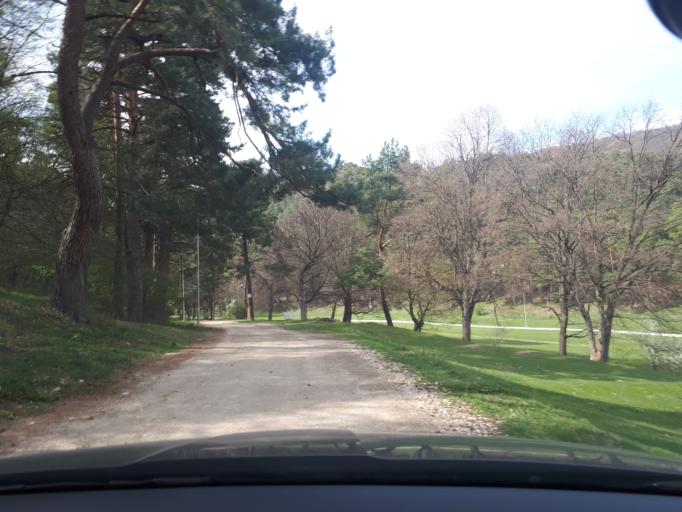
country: RO
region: Brasov
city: Codlea
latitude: 45.7057
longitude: 25.4363
